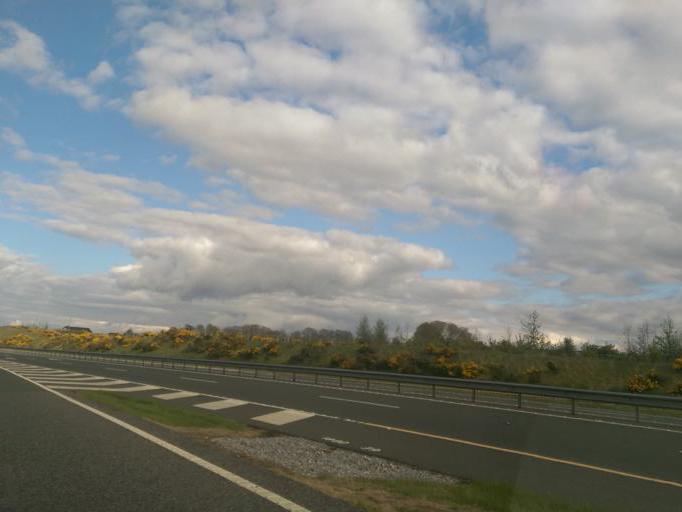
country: IE
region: Connaught
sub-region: County Galway
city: Ballinasloe
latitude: 53.3142
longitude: -8.1748
